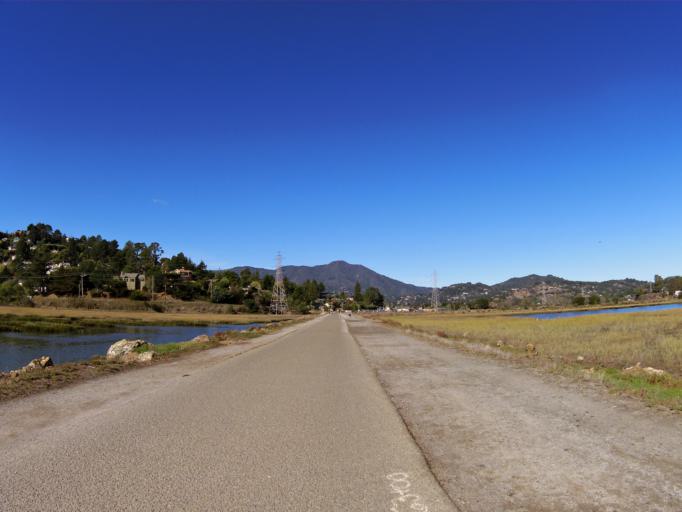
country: US
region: California
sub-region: Marin County
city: Tamalpais-Homestead Valley
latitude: 37.8846
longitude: -122.5213
